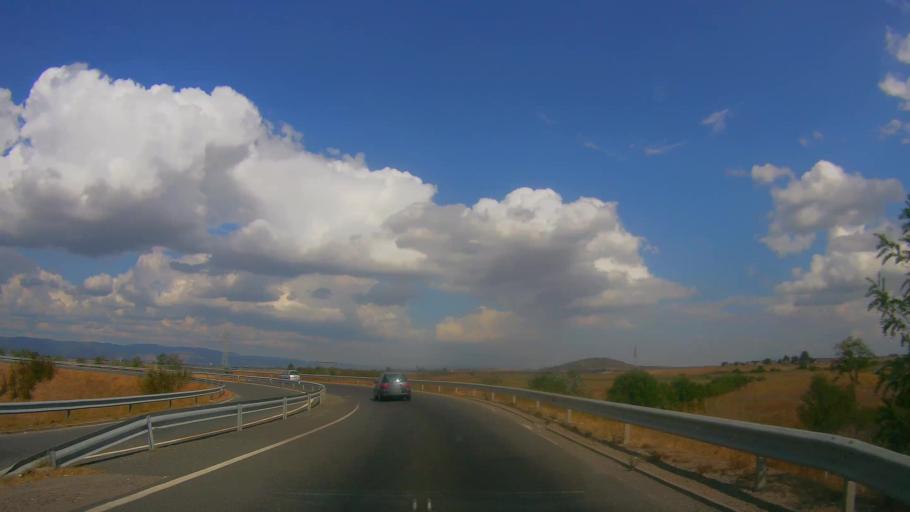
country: BG
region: Yambol
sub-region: Obshtina Yambol
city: Yambol
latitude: 42.5367
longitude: 26.4198
